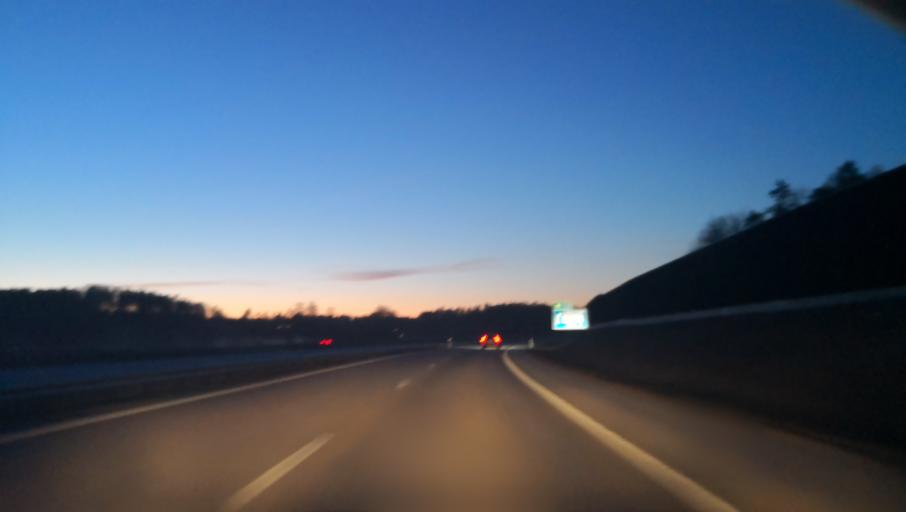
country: SE
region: Stockholm
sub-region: Nynashamns Kommun
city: Osmo
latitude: 58.9501
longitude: 17.9018
